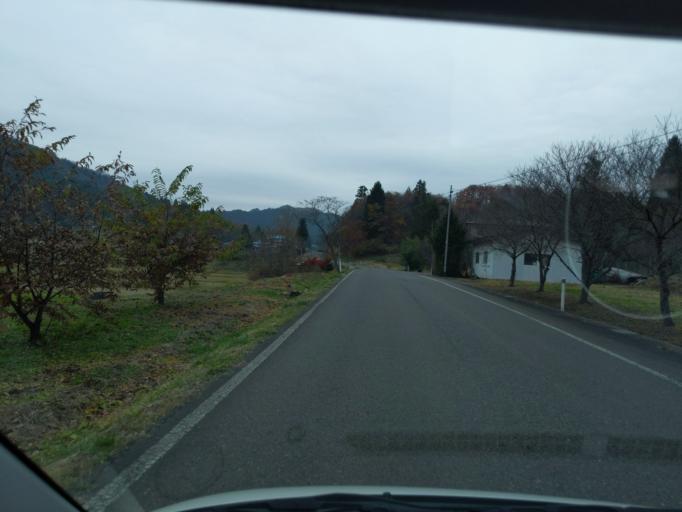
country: JP
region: Iwate
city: Kitakami
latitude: 39.2726
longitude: 141.1769
